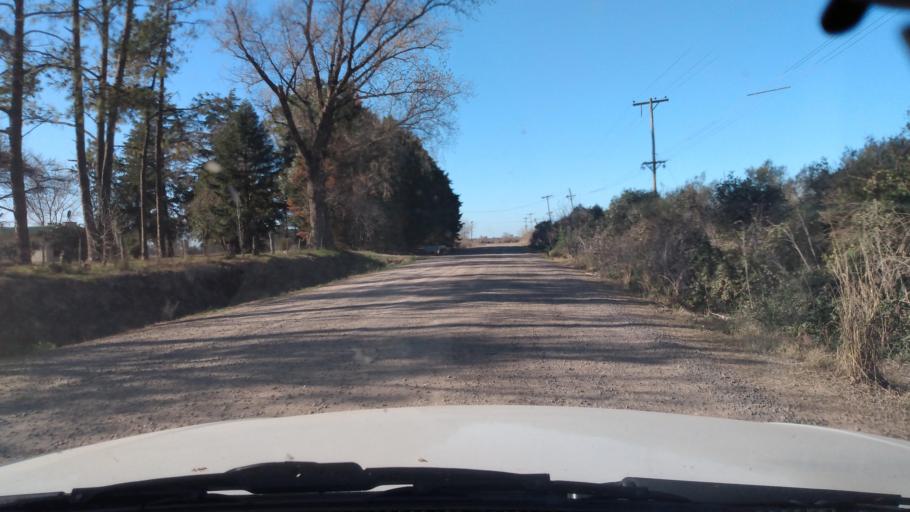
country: AR
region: Buenos Aires
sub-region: Partido de Mercedes
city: Mercedes
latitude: -34.6414
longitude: -59.3739
